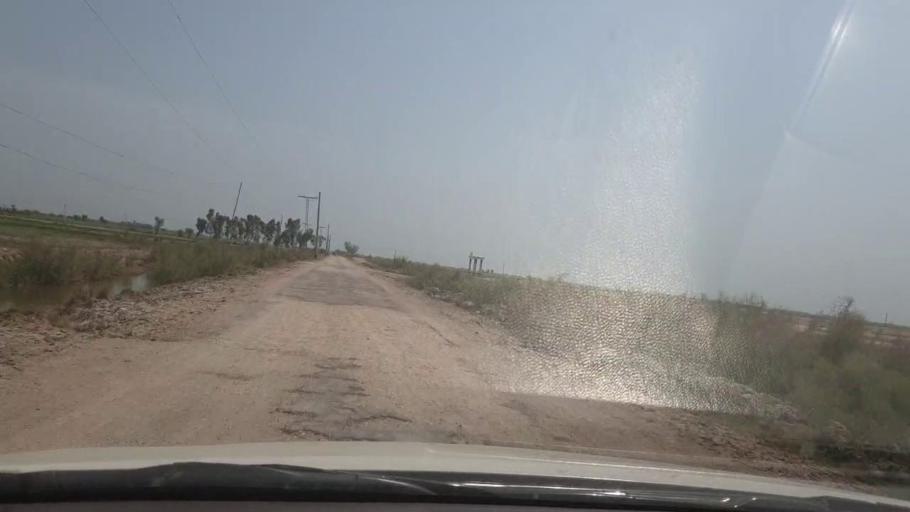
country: PK
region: Sindh
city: Garhi Yasin
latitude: 27.9593
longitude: 68.5050
